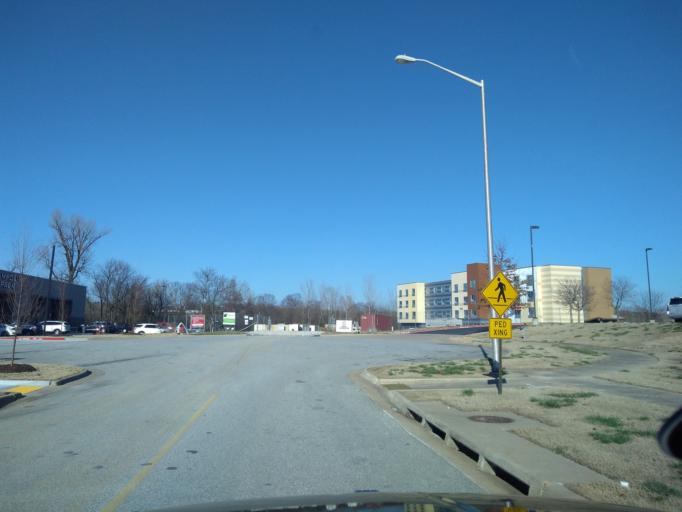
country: US
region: Arkansas
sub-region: Washington County
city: Johnson
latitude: 36.1184
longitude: -94.1480
